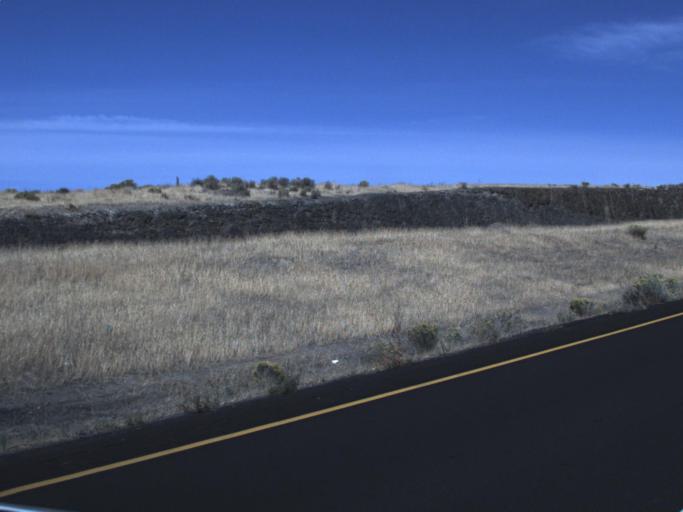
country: US
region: Washington
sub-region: Benton County
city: Benton City
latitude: 46.2542
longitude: -119.4626
